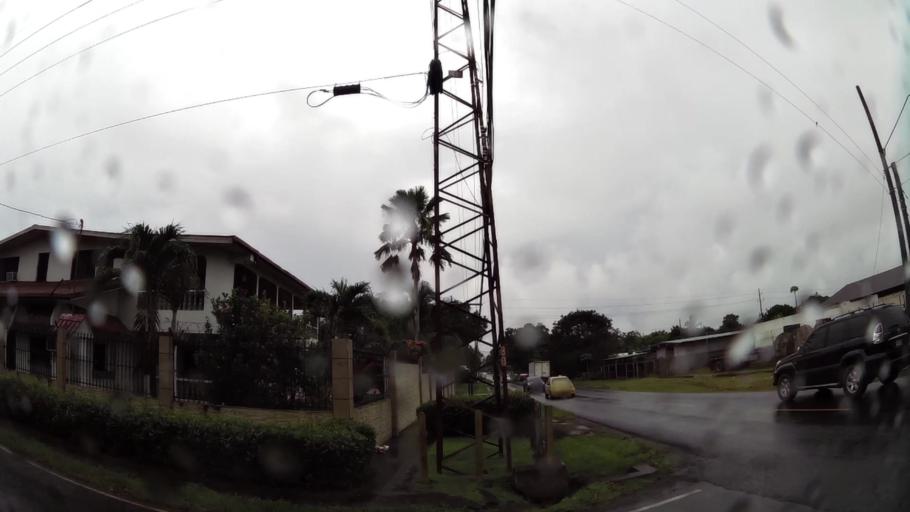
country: PA
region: Chiriqui
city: David
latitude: 8.4366
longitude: -82.4343
